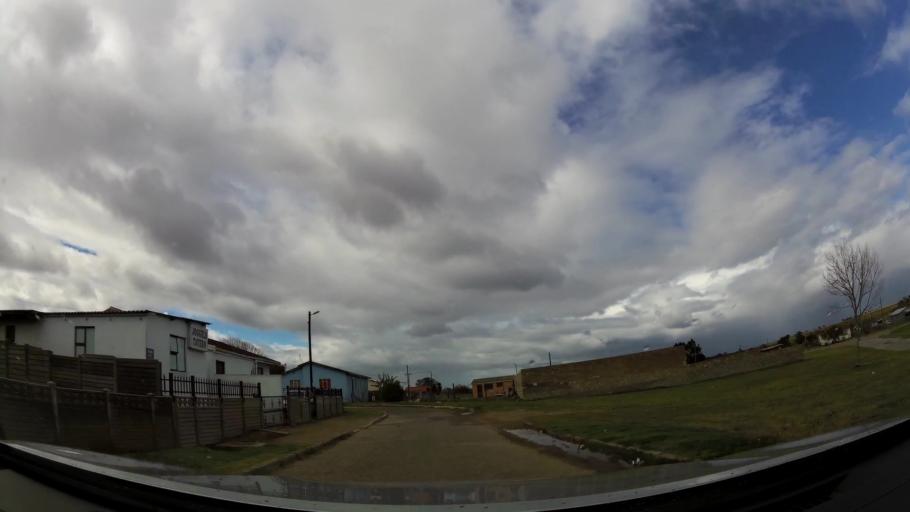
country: ZA
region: Western Cape
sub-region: Eden District Municipality
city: George
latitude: -34.0225
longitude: 22.4692
